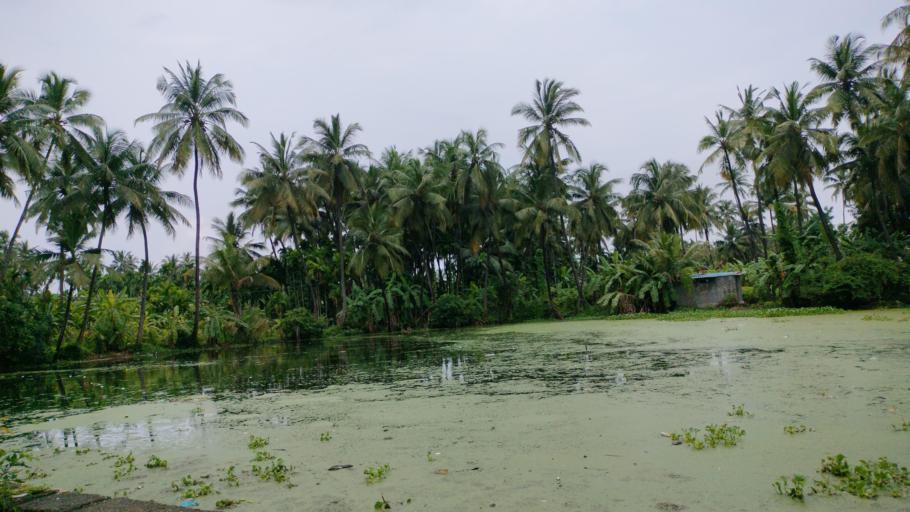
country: IN
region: Maharashtra
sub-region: Thane
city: Virar
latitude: 19.4567
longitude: 72.7685
